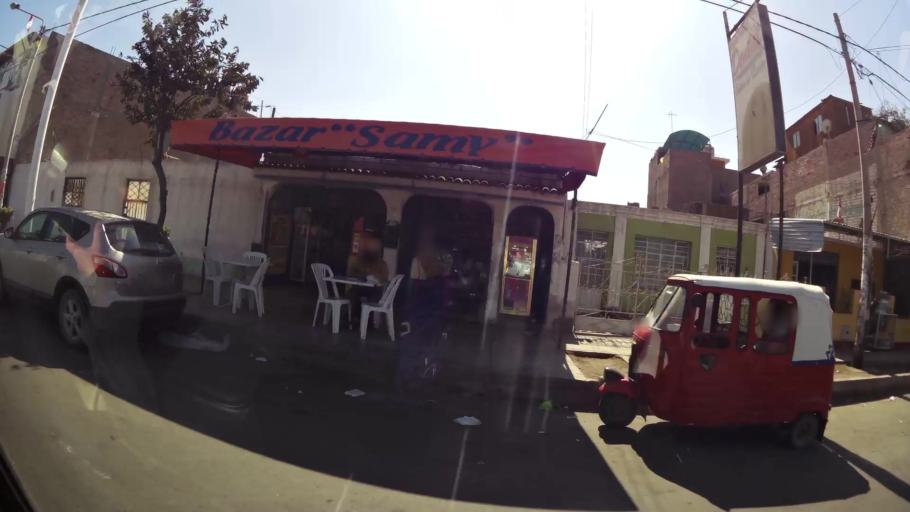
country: PE
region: Ica
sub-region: Provincia de Ica
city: La Tinguina
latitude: -14.0484
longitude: -75.7052
